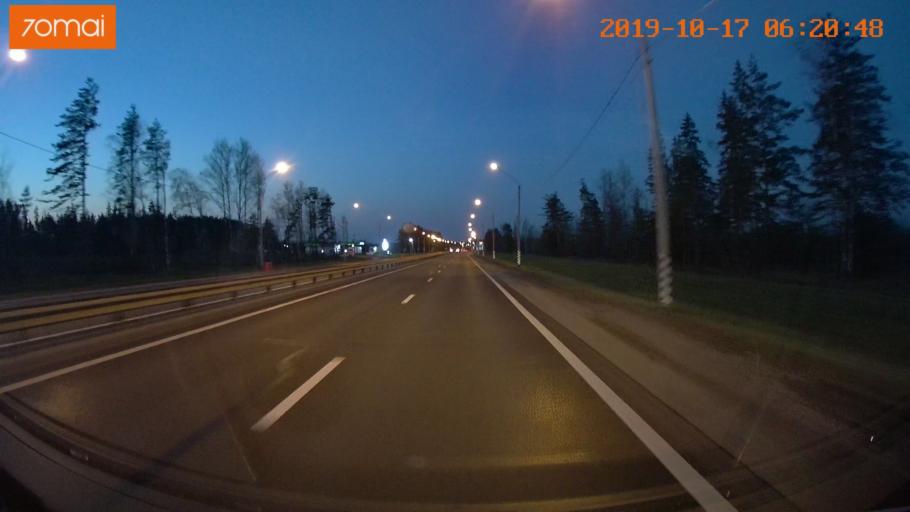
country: RU
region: Ivanovo
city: Lezhnevo
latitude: 56.8108
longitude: 40.8876
